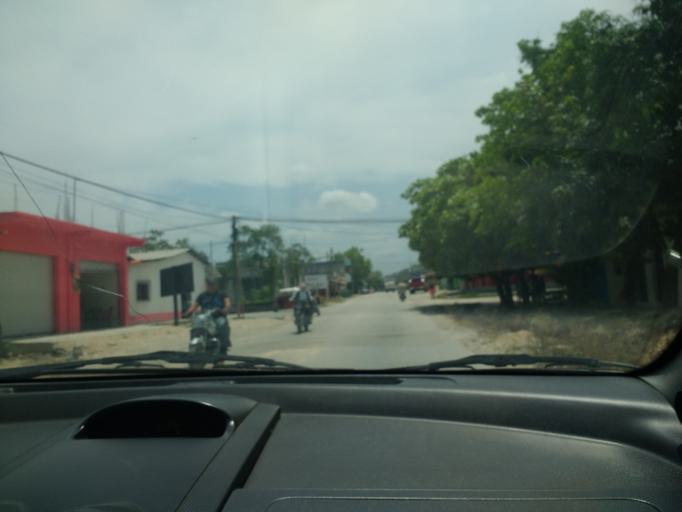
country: GT
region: Peten
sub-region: Municipio de San Benito
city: San Benito
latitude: 16.9191
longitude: -89.9108
